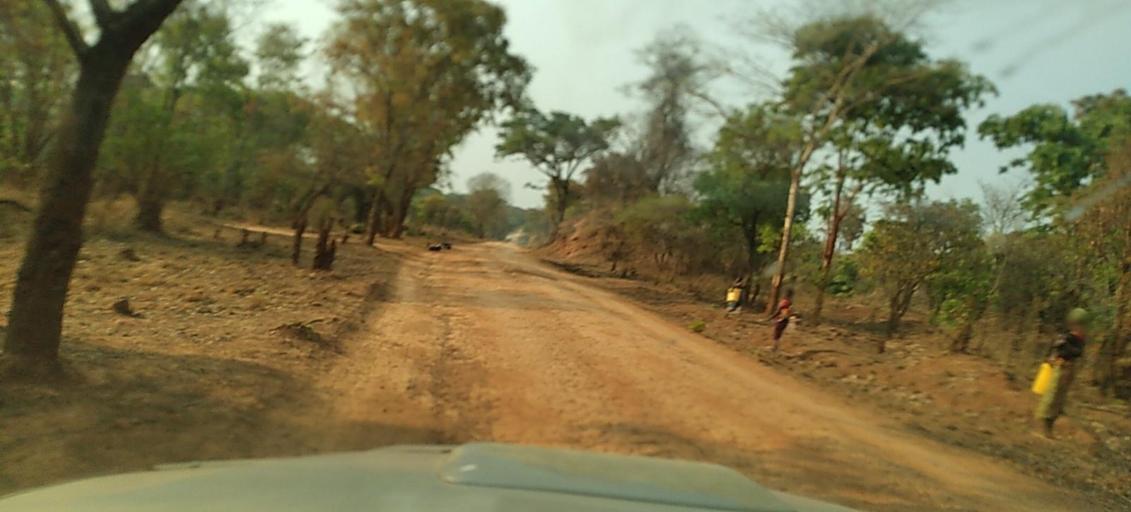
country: ZM
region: North-Western
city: Kasempa
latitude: -13.2862
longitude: 26.5550
